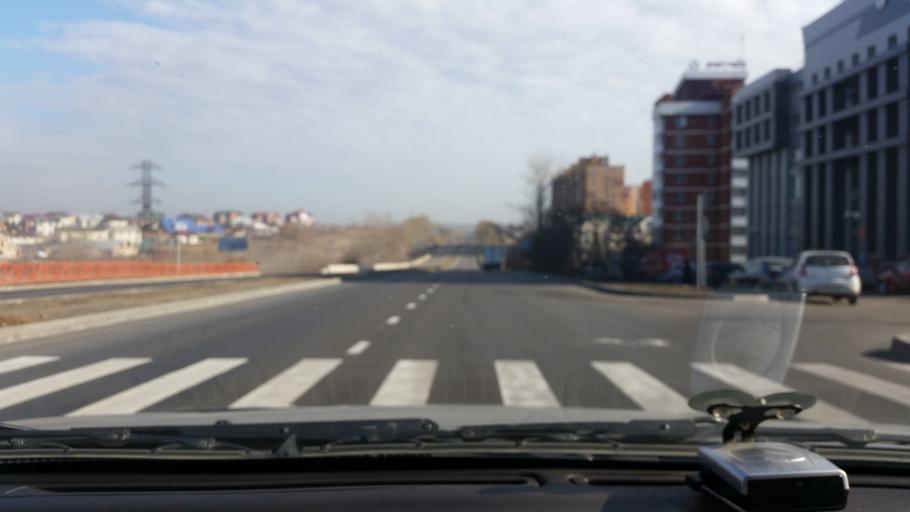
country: RU
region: Irkutsk
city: Dzerzhinsk
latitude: 52.2601
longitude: 104.3578
